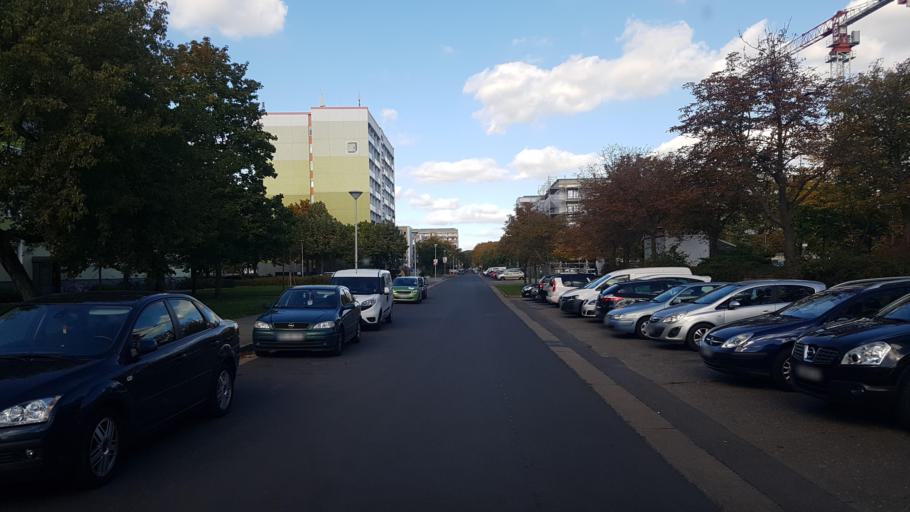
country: DE
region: Brandenburg
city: Cottbus
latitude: 51.7614
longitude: 14.3171
